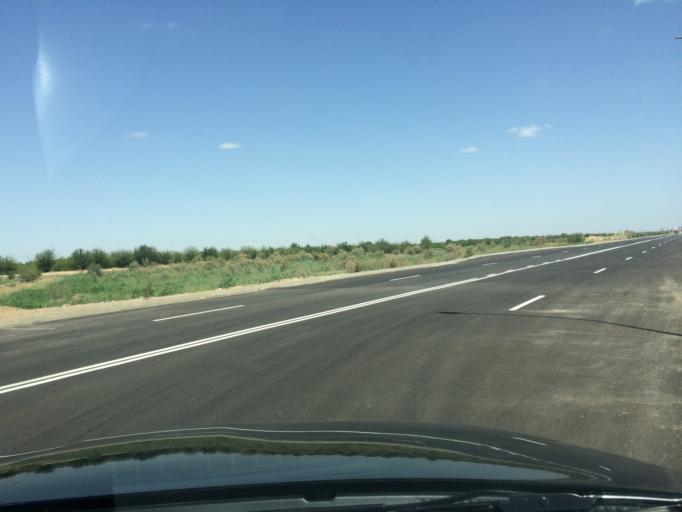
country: TM
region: Ahal
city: Abadan
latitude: 38.1000
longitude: 58.2830
